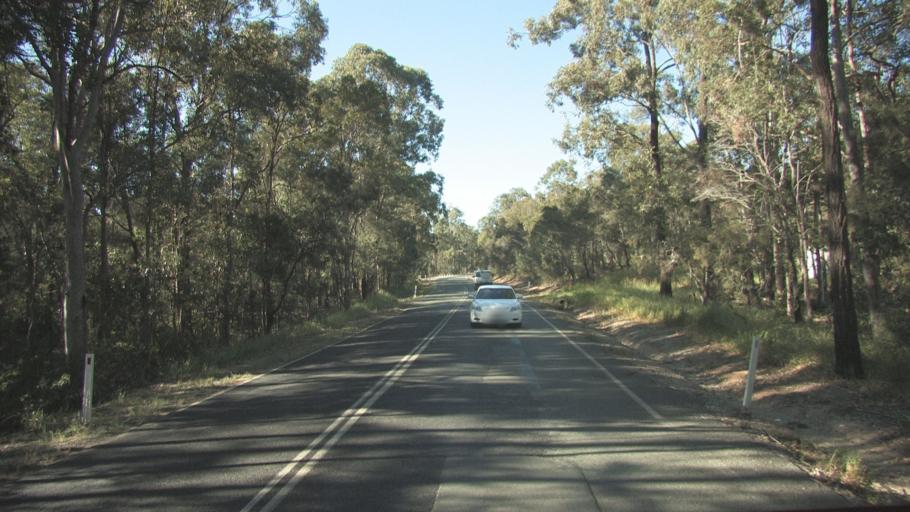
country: AU
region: Queensland
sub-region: Logan
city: Logan Reserve
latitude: -27.7473
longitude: 153.1334
